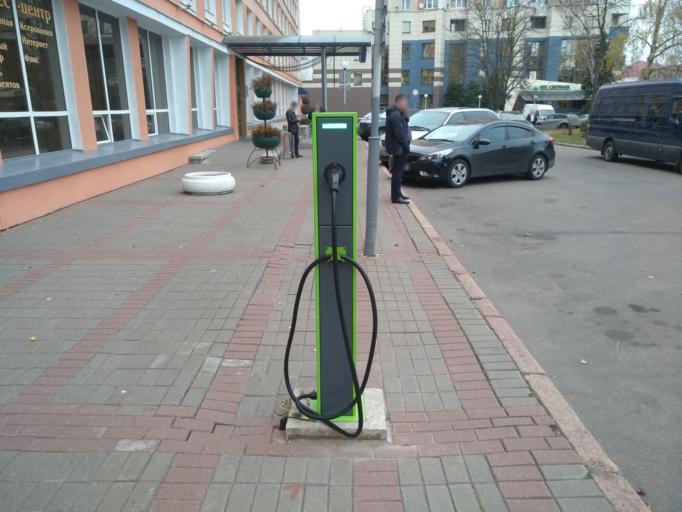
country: BY
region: Minsk
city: Minsk
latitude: 53.8783
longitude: 27.5335
